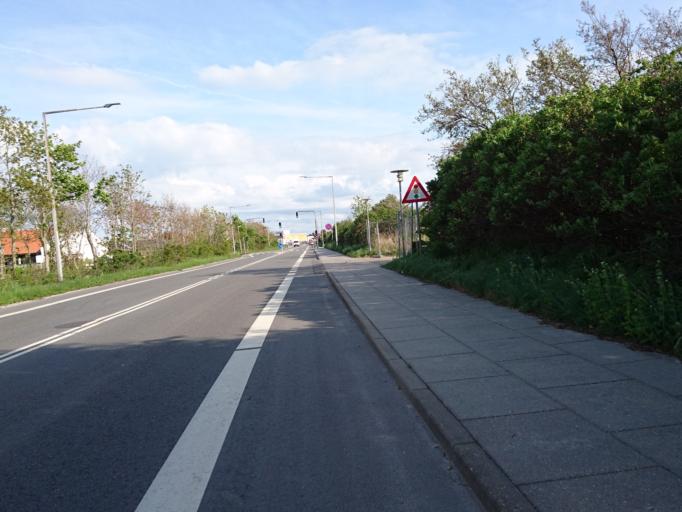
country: DK
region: North Denmark
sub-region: Frederikshavn Kommune
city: Skagen
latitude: 57.7280
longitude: 10.5595
